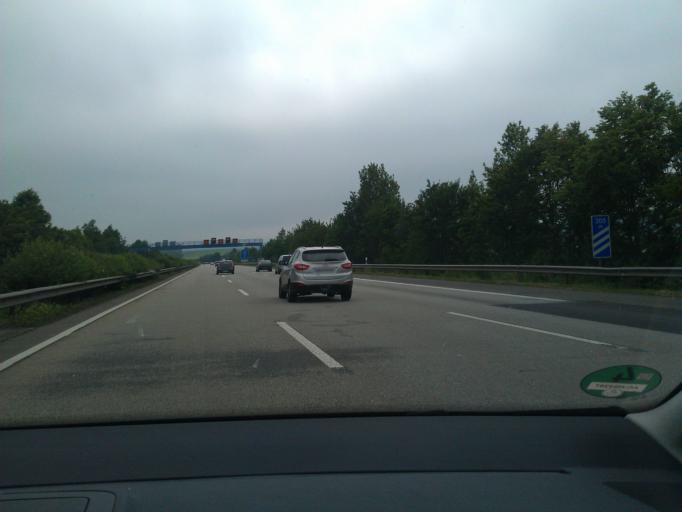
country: DE
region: Rheinland-Pfalz
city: Niederzissen
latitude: 50.4480
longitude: 7.2290
